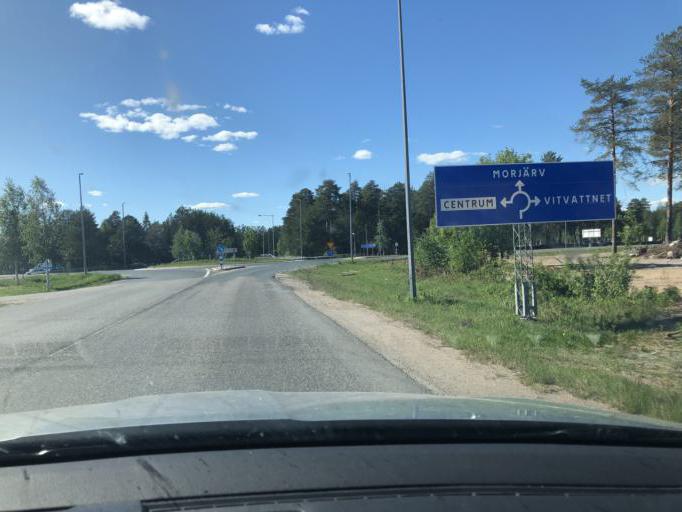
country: SE
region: Norrbotten
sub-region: Kalix Kommun
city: Kalix
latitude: 65.8633
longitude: 23.1405
